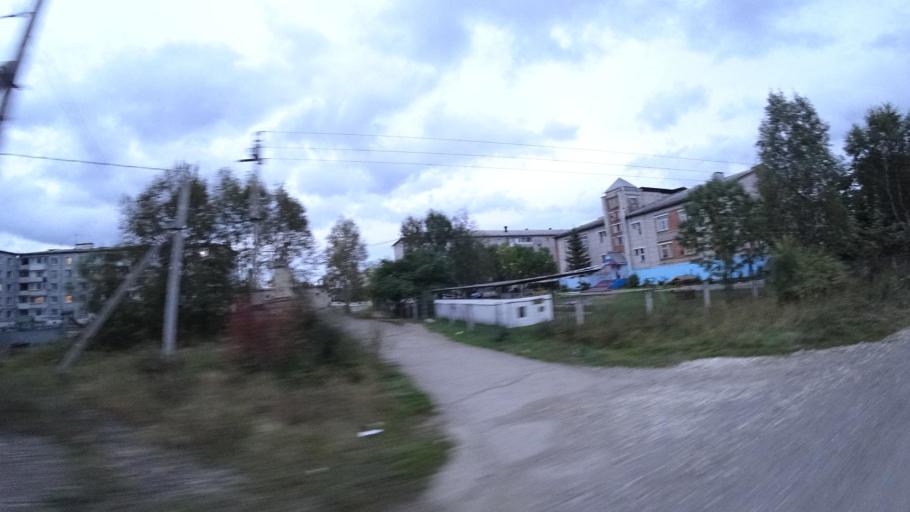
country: RU
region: Jewish Autonomous Oblast
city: Izvestkovyy
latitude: 48.9827
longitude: 131.5538
